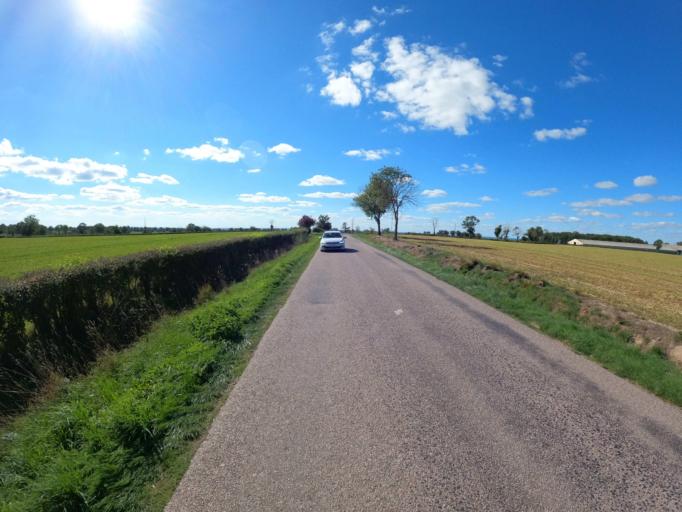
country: FR
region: Auvergne
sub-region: Departement de l'Allier
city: Buxieres-les-Mines
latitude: 46.4032
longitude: 2.9779
